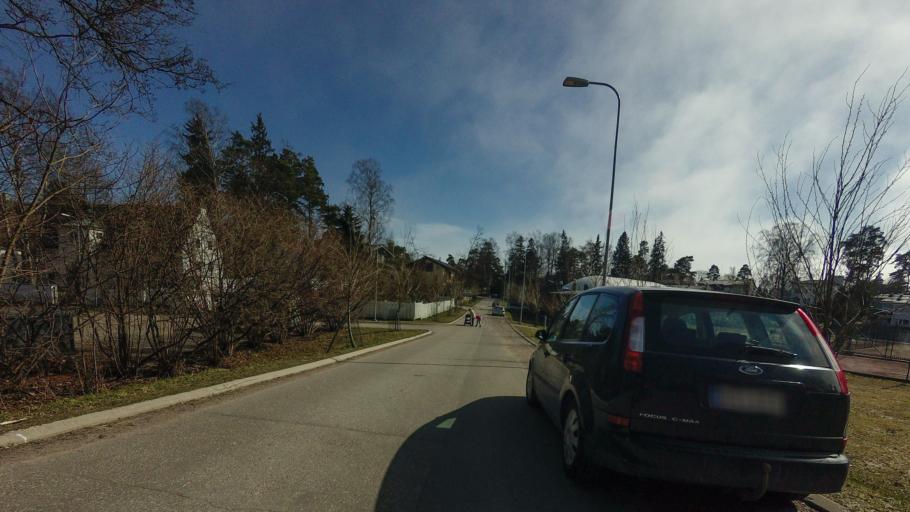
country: FI
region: Uusimaa
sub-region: Helsinki
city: Helsinki
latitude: 60.1823
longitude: 25.0138
